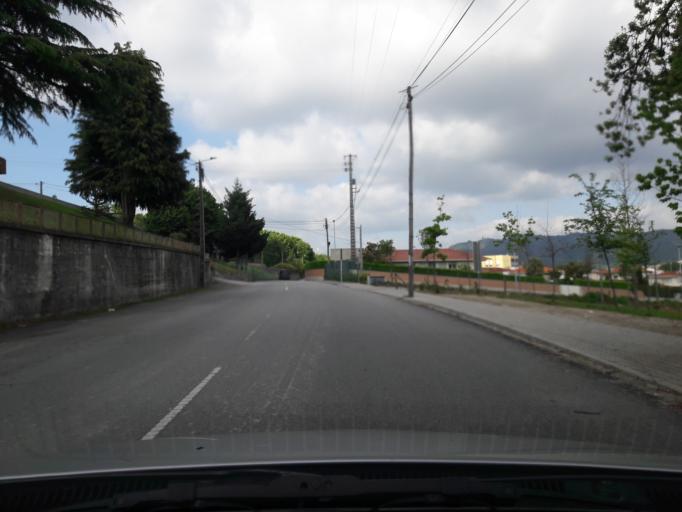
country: PT
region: Braga
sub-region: Guimaraes
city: Candoso
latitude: 41.4201
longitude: -8.3192
